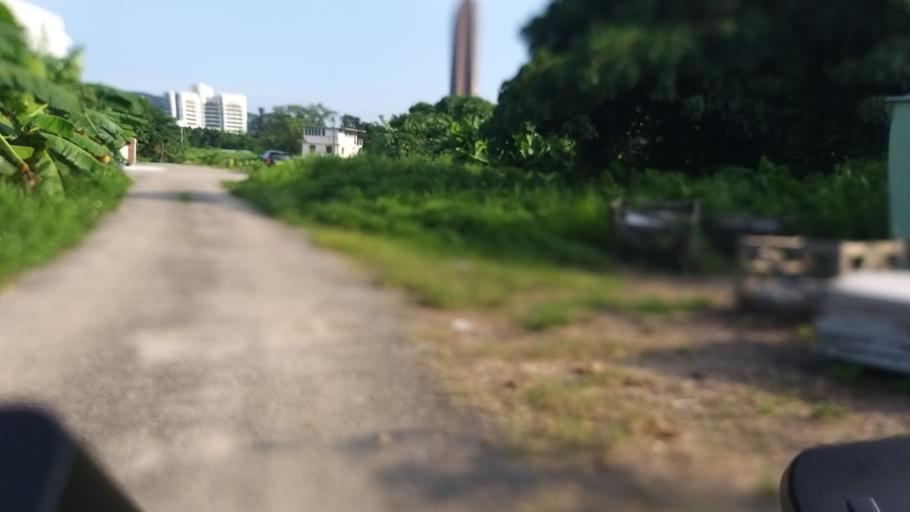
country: HK
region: Yuen Long
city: Yuen Long Kau Hui
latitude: 22.4534
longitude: 114.0398
